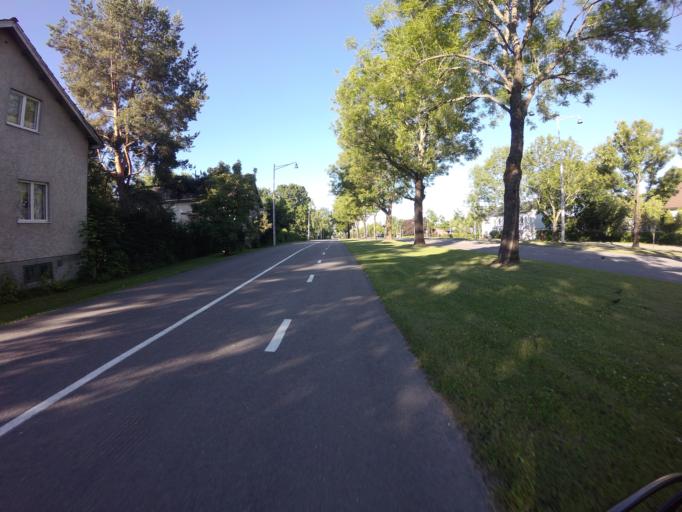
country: FI
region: Varsinais-Suomi
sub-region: Turku
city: Turku
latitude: 60.4698
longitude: 22.2805
